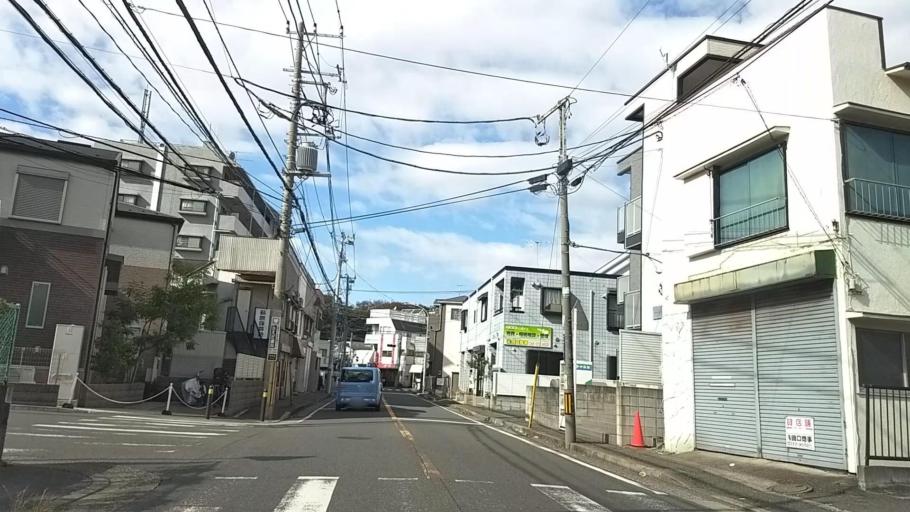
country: JP
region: Kanagawa
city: Yokohama
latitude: 35.5049
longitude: 139.6488
